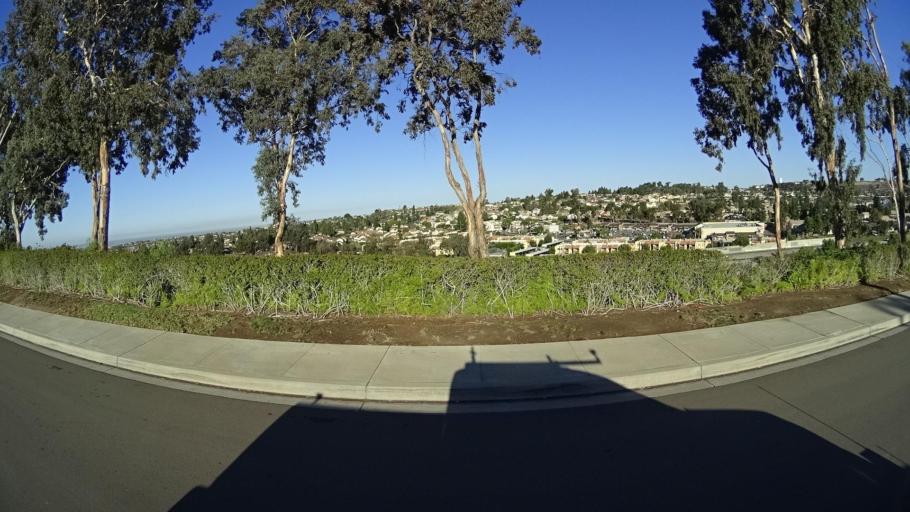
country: US
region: California
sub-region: San Diego County
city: Bonita
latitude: 32.6741
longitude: -117.0359
